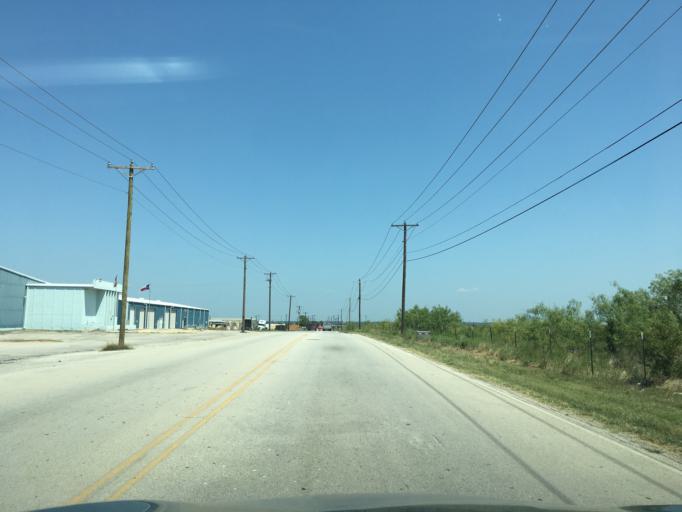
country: US
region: Texas
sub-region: Tarrant County
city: Crowley
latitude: 32.6141
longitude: -97.3365
